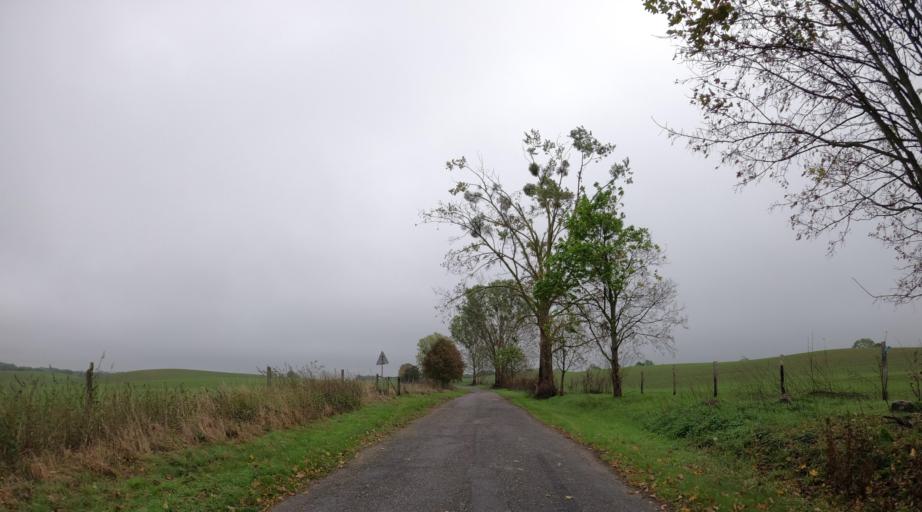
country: PL
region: West Pomeranian Voivodeship
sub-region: Powiat mysliborski
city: Mysliborz
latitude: 52.8938
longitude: 14.7810
